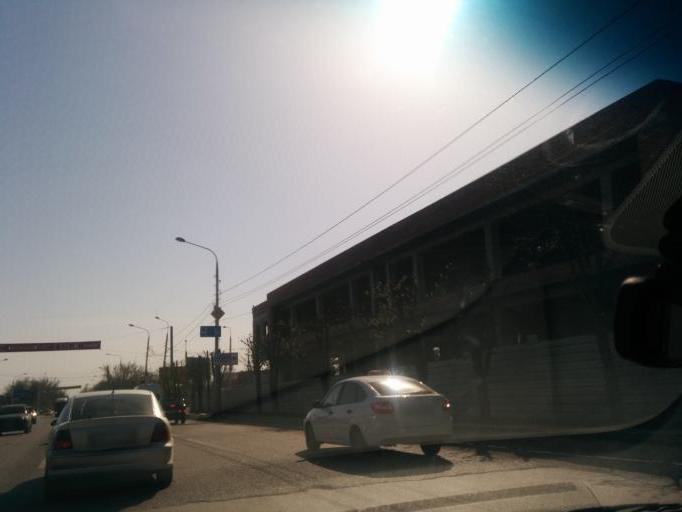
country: RU
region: Rostov
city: Shakhty
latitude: 47.6993
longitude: 40.2089
